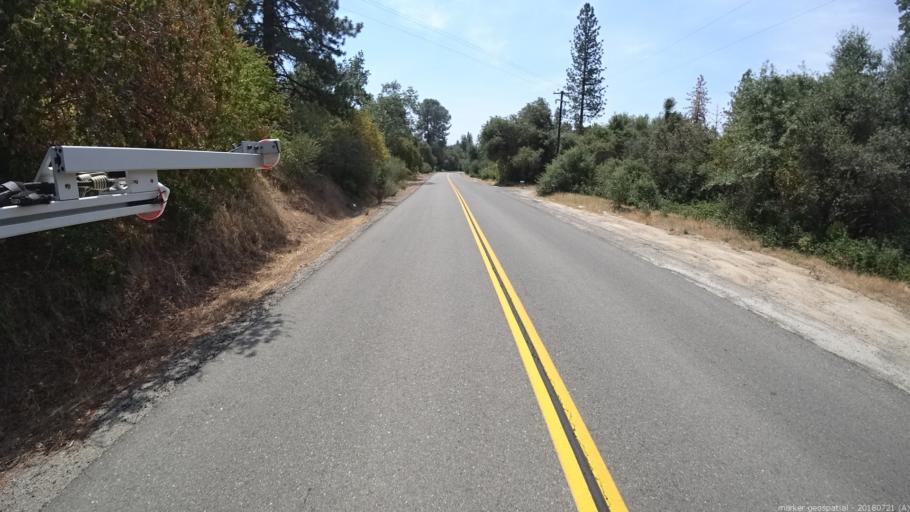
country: US
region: California
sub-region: Madera County
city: Oakhurst
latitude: 37.2546
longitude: -119.5381
